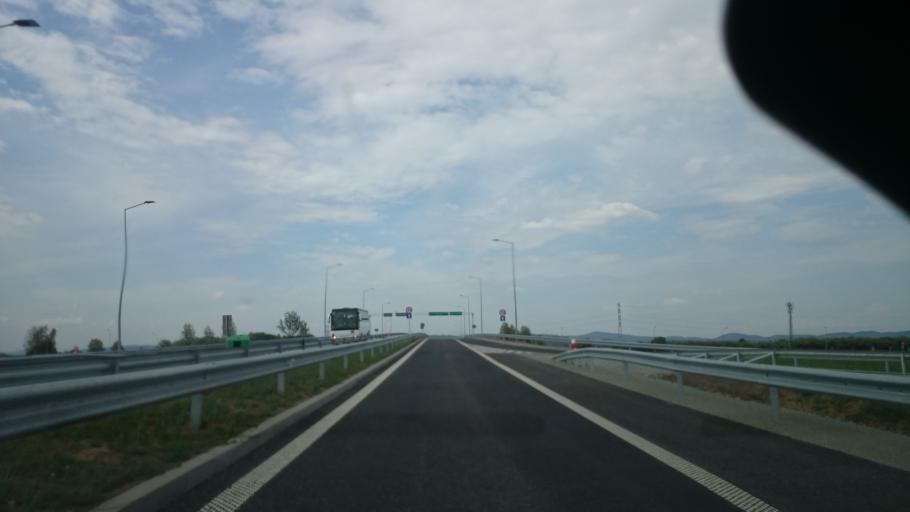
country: PL
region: Lower Silesian Voivodeship
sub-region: Powiat klodzki
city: Klodzko
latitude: 50.4369
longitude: 16.6276
